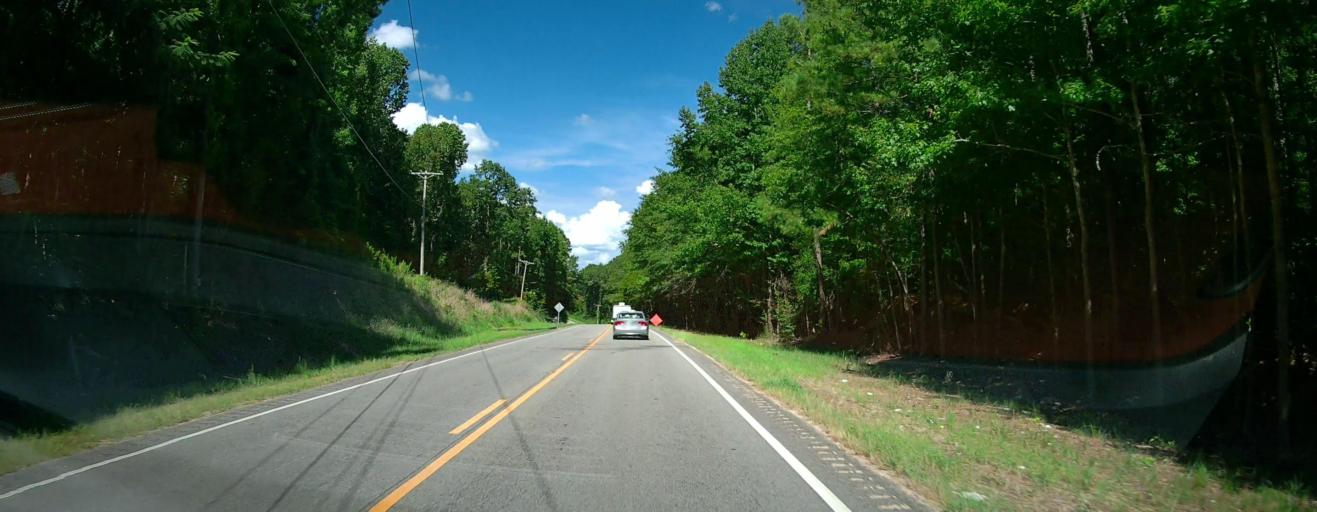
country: US
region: Alabama
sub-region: Macon County
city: Tuskegee
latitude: 32.3757
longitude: -85.8361
